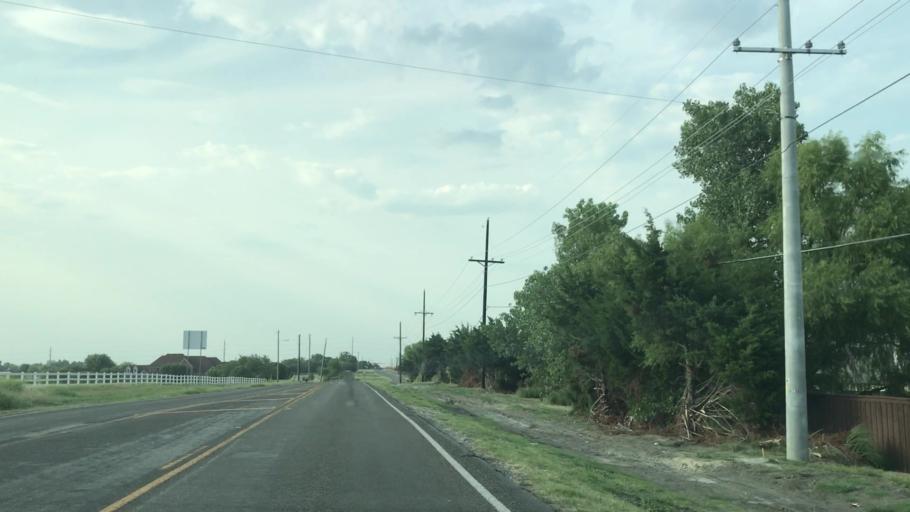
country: US
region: Texas
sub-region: Rockwall County
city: Fate
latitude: 32.9287
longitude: -96.4183
